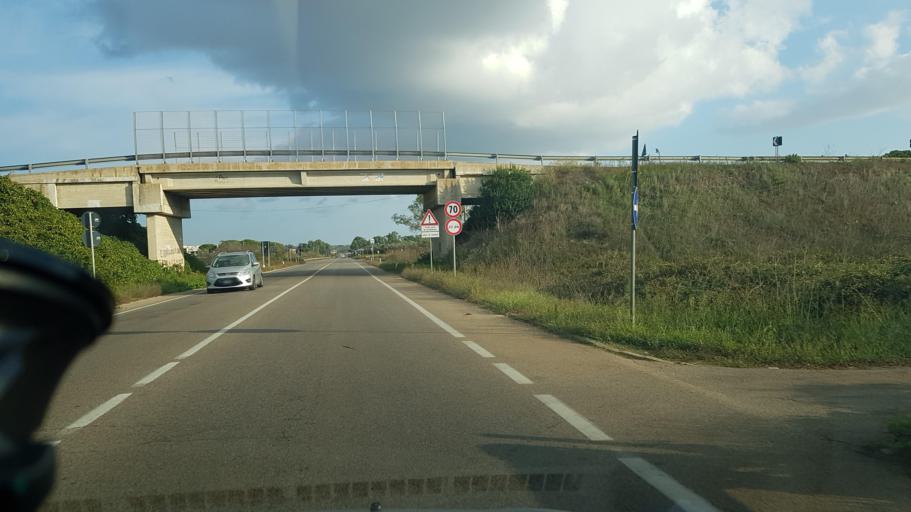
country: IT
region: Apulia
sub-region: Provincia di Lecce
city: Acquarica del Capo
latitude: 39.9013
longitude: 18.2487
